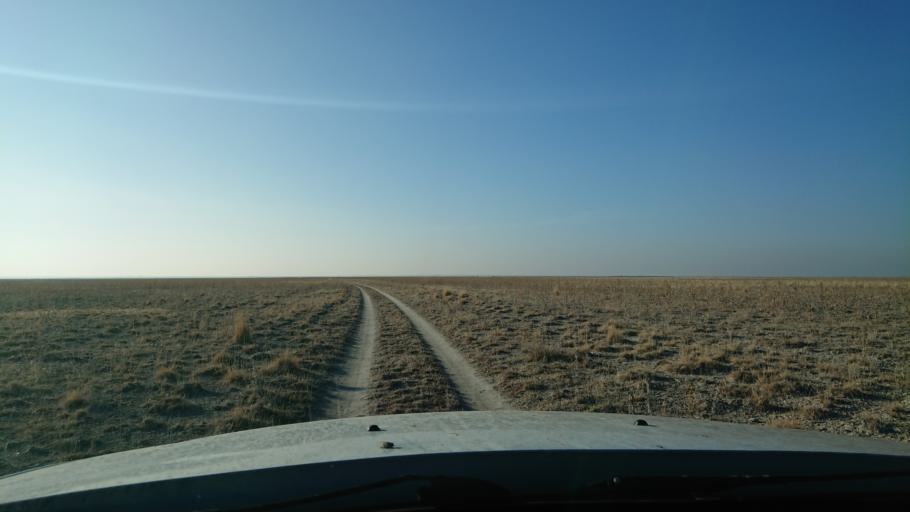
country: TR
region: Aksaray
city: Sultanhani
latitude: 38.3716
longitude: 33.5515
